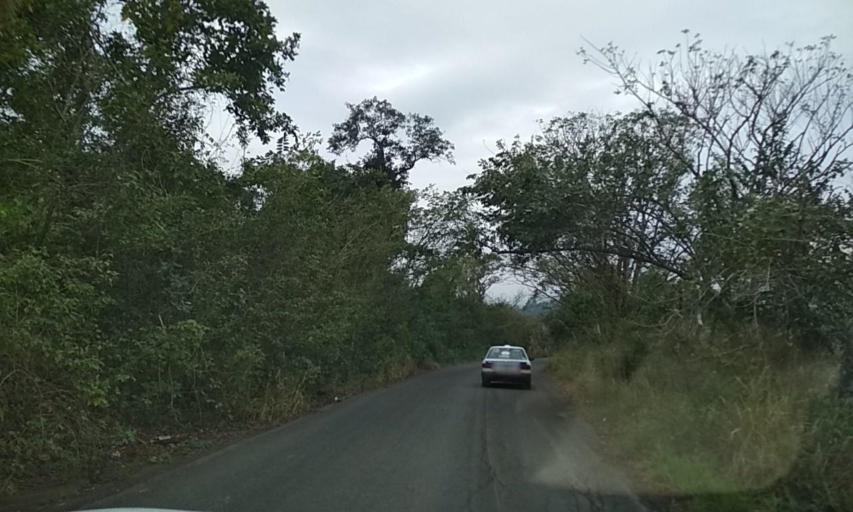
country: MX
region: Veracruz
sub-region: Coatzintla
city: Manuel Maria Contreras
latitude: 20.4410
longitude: -97.5068
